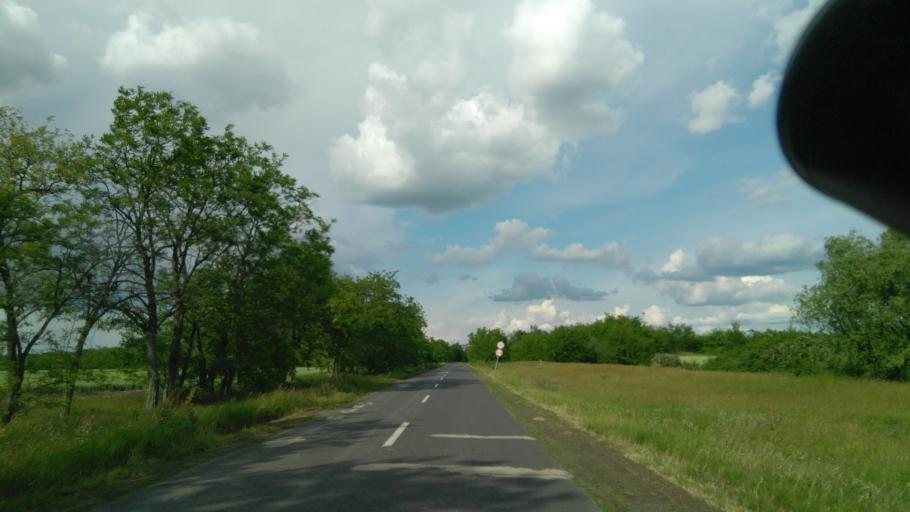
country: HU
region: Bekes
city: Dombegyhaz
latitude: 46.3153
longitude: 21.0770
